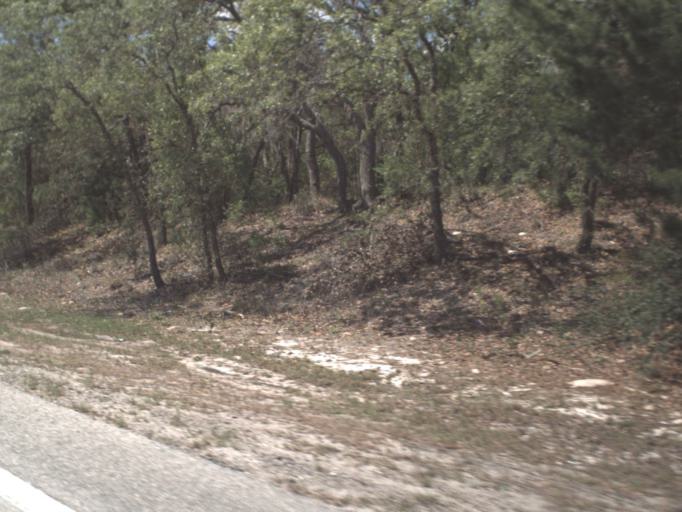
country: US
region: Florida
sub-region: Flagler County
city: Palm Coast
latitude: 29.6464
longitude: -81.2865
